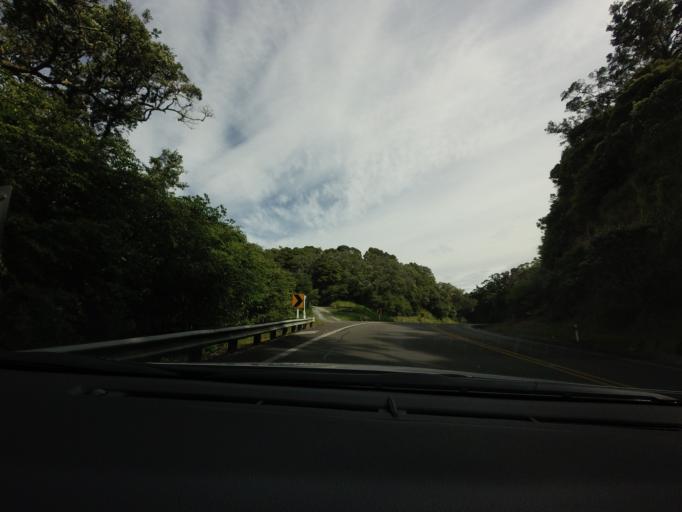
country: NZ
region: Auckland
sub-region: Auckland
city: Warkworth
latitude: -36.5492
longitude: 174.7063
